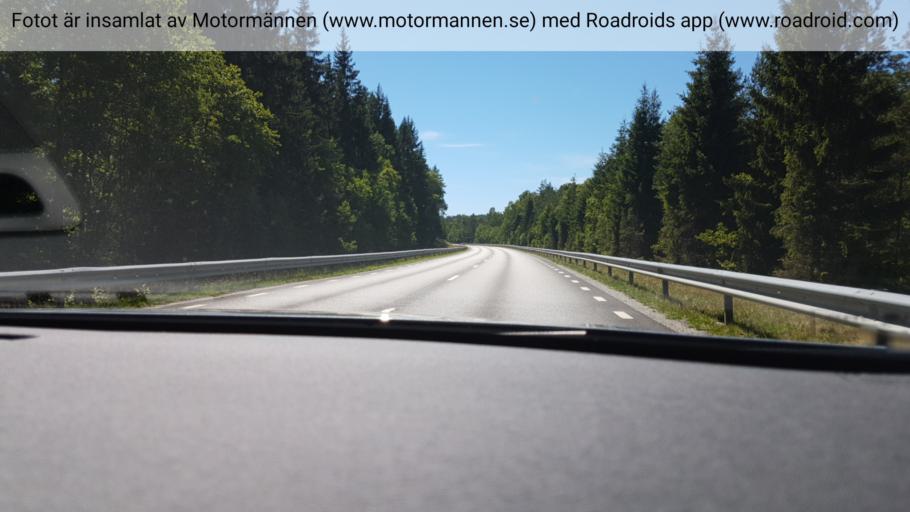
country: SE
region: Joenkoeping
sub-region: Gnosjo Kommun
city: Gnosjoe
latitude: 57.5936
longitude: 13.7343
